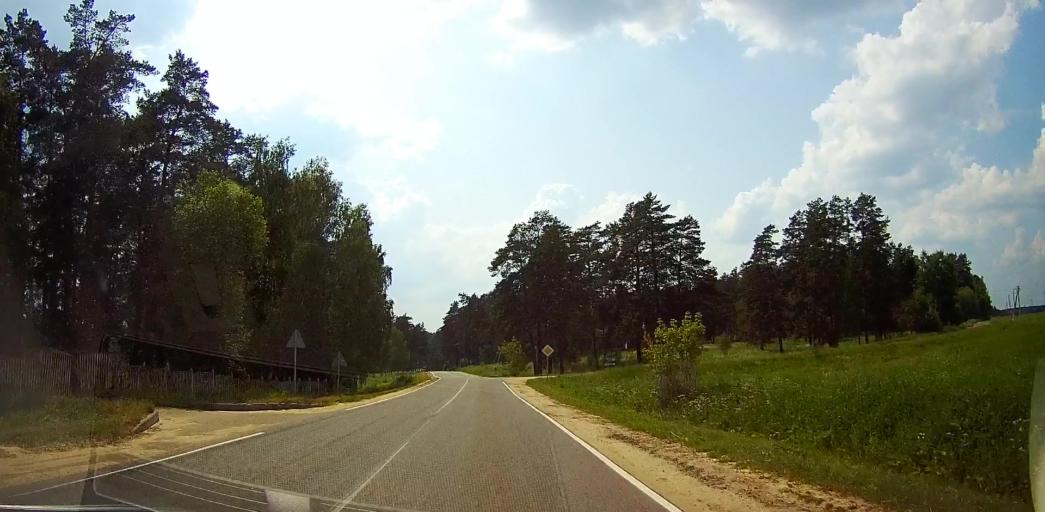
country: RU
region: Moskovskaya
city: Zhilevo
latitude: 55.0557
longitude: 38.0507
